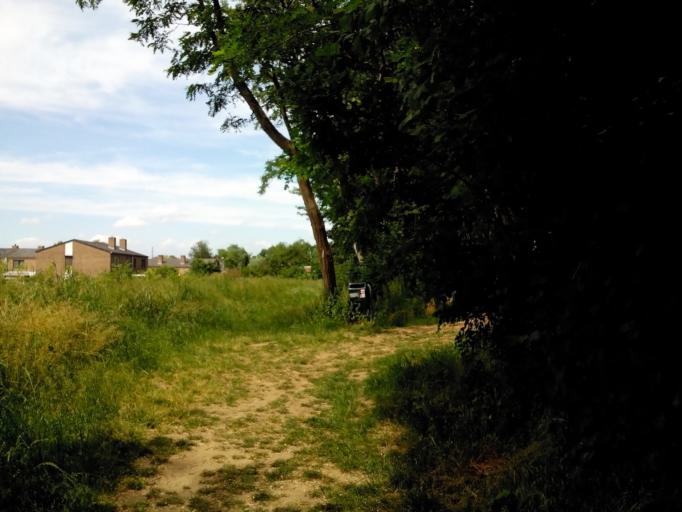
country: BE
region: Flanders
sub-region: Provincie Vlaams-Brabant
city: Leuven
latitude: 50.9059
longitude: 4.7215
